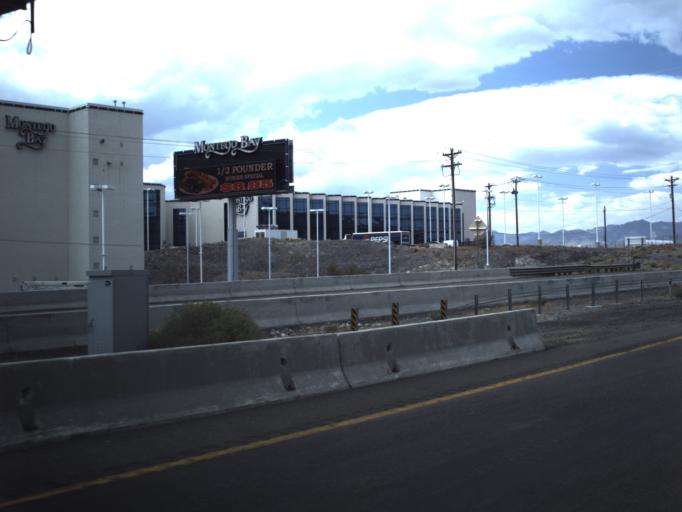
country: US
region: Utah
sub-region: Tooele County
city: Wendover
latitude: 40.7382
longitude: -114.0436
